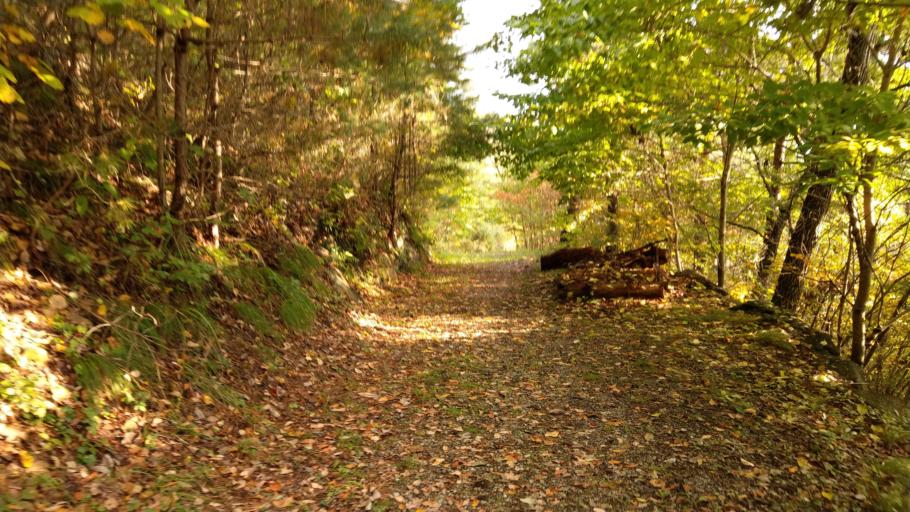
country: JP
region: Nagano
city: Komoro
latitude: 36.3445
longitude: 138.4181
